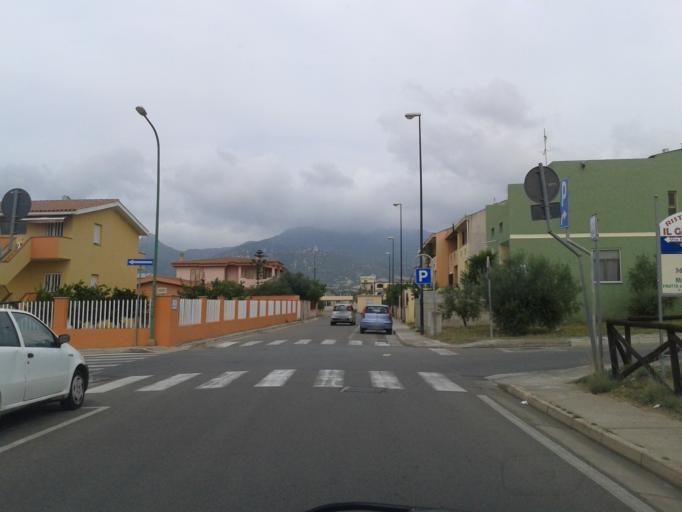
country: IT
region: Sardinia
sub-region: Provincia di Cagliari
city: Villasimius
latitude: 39.1473
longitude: 9.5186
